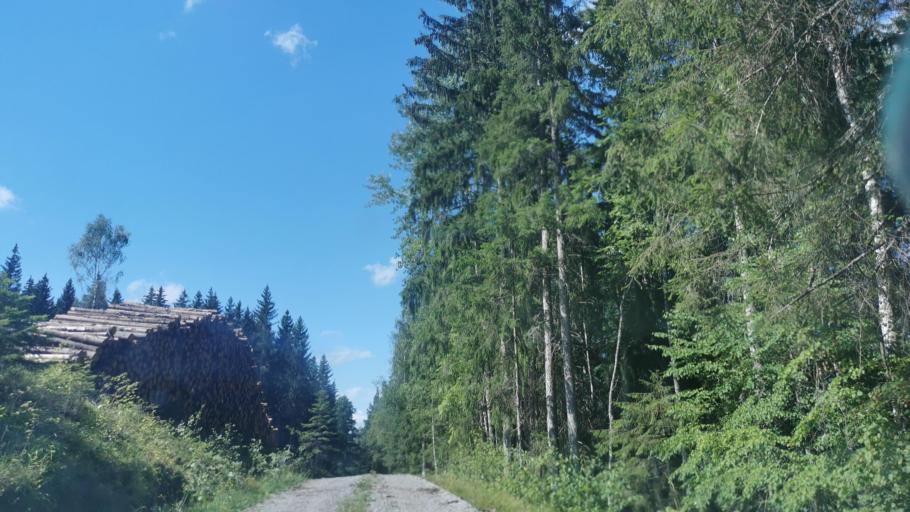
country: SE
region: OEstergoetland
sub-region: Finspangs Kommun
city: Finspang
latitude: 58.7917
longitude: 15.8341
